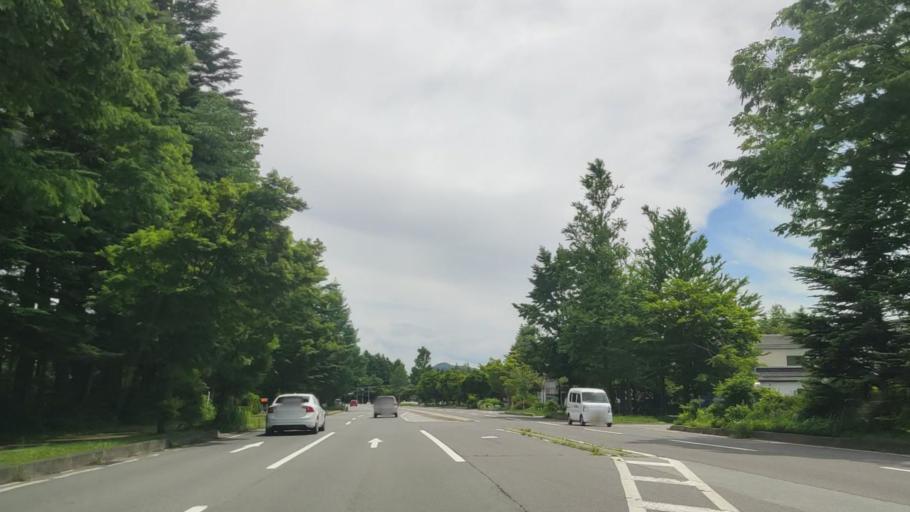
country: JP
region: Nagano
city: Saku
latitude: 36.3347
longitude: 138.6313
